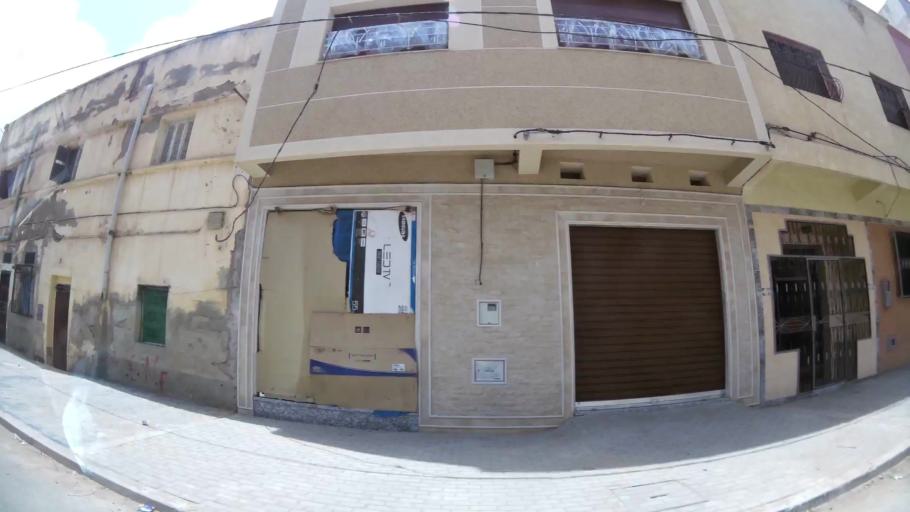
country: MA
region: Oriental
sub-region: Nador
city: Nador
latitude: 35.1717
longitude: -2.9190
